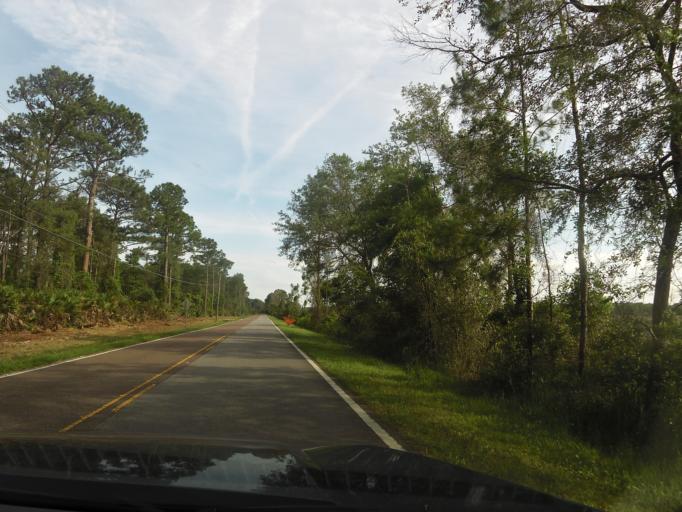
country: US
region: Florida
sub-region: Nassau County
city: Fernandina Beach
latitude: 30.5099
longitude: -81.4753
